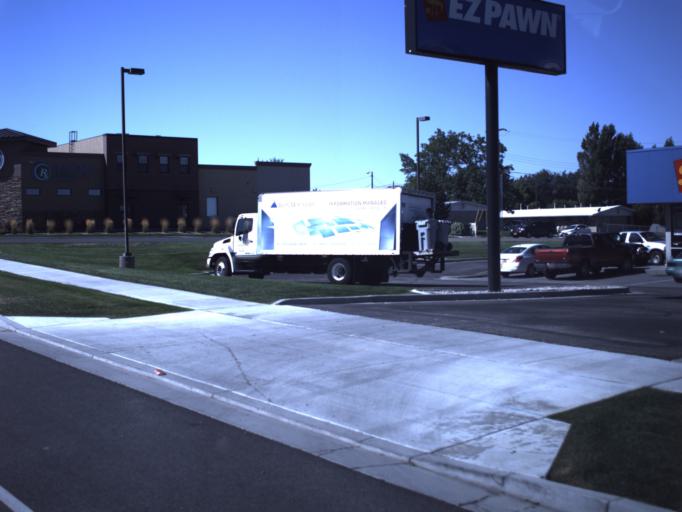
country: US
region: Utah
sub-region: Tooele County
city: Tooele
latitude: 40.5410
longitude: -112.2985
